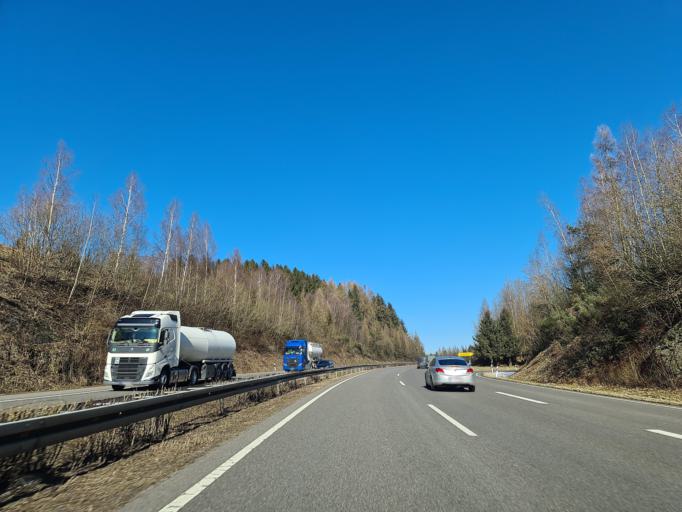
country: DE
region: Saxony
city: Gornau
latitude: 50.7619
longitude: 13.0152
